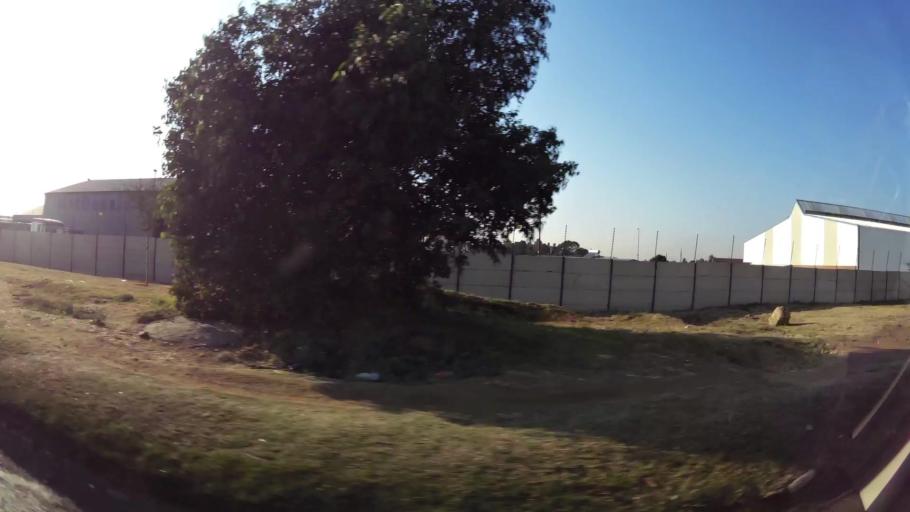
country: ZA
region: Gauteng
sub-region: City of Johannesburg Metropolitan Municipality
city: Modderfontein
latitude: -26.1540
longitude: 28.2021
